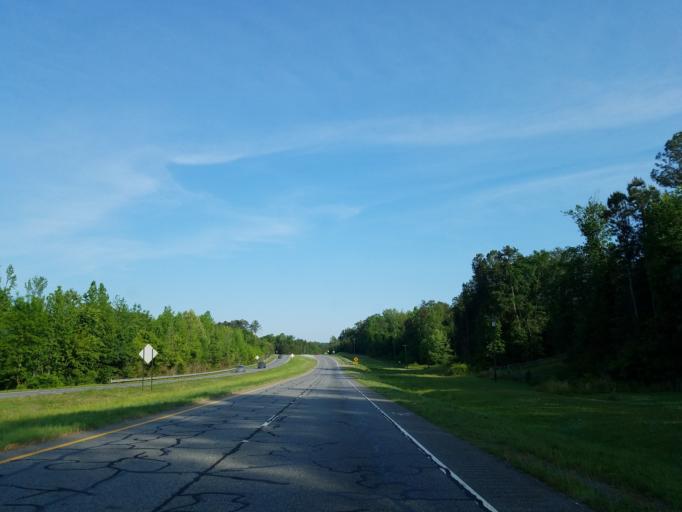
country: US
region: Georgia
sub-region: Chattooga County
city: Summerville
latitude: 34.4563
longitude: -85.2549
